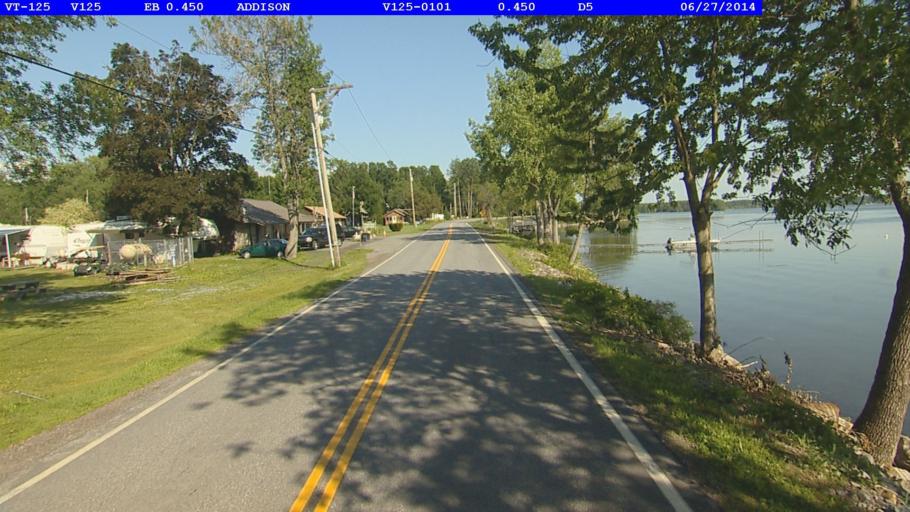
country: US
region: New York
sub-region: Essex County
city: Port Henry
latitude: 44.0332
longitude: -73.4106
